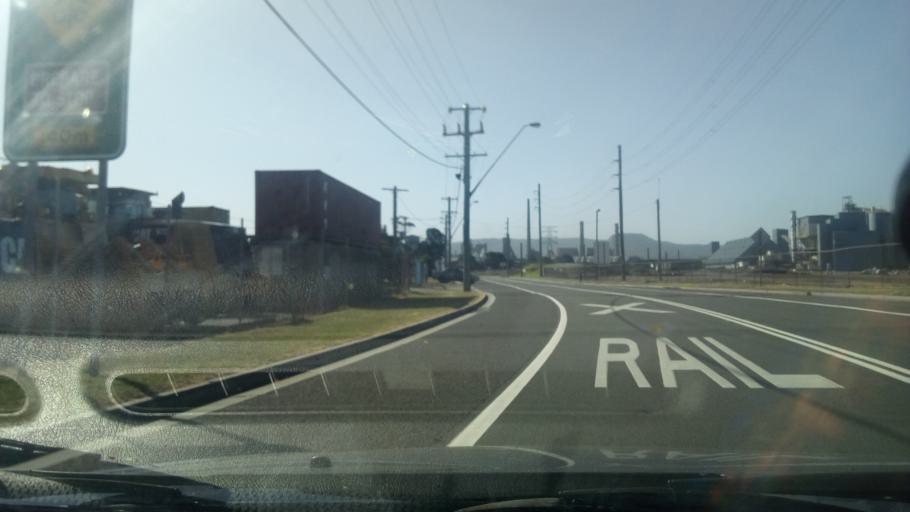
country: AU
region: New South Wales
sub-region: Wollongong
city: Port Kembla
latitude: -34.4763
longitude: 150.9038
